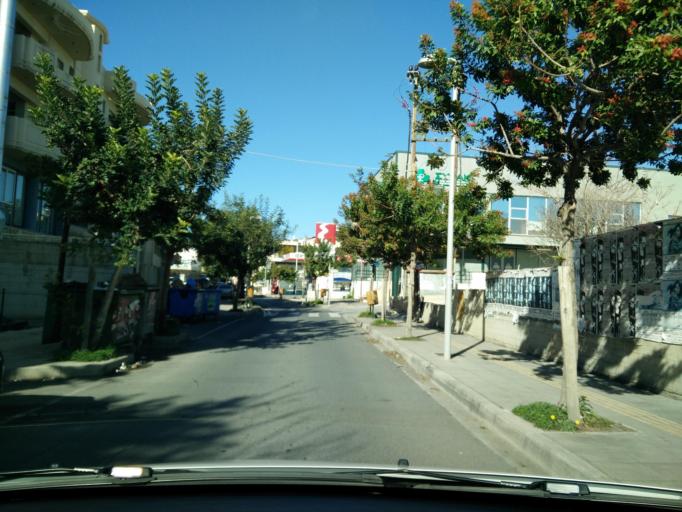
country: GR
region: Crete
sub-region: Nomos Irakleiou
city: Nea Alikarnassos
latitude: 35.3351
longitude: 25.1582
